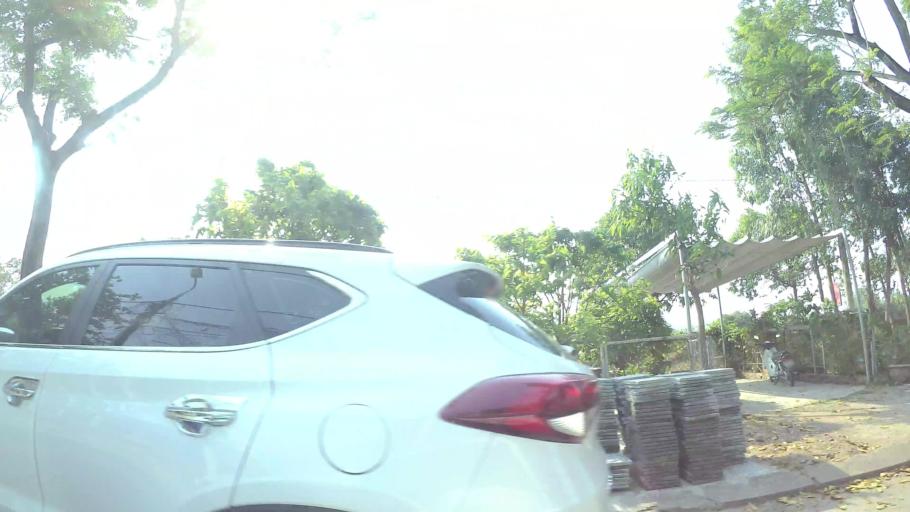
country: VN
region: Da Nang
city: Cam Le
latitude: 16.0073
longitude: 108.1924
